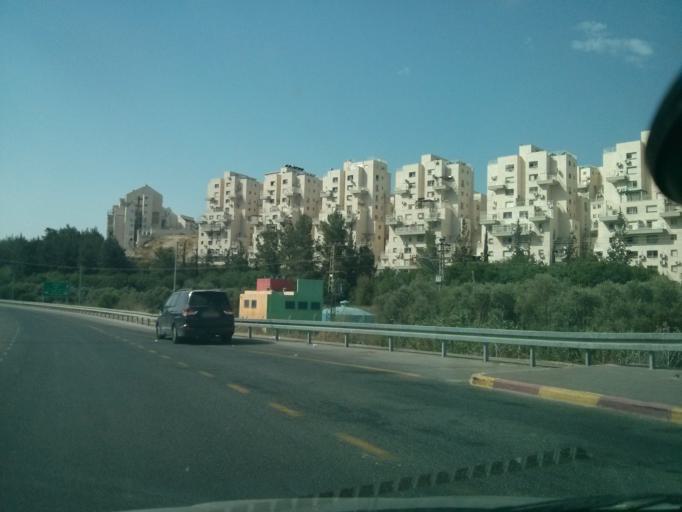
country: IL
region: Jerusalem
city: Bet Shemesh
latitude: 31.7516
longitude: 35.0008
